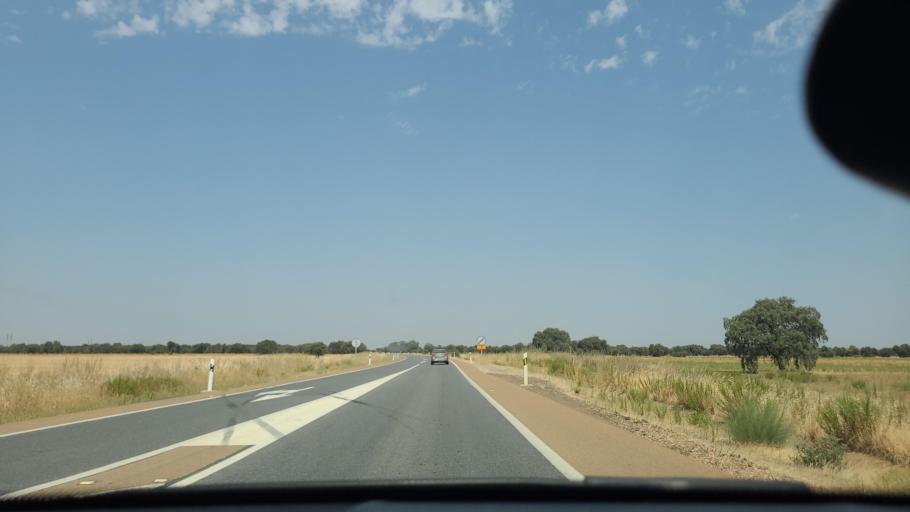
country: ES
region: Extremadura
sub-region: Provincia de Badajoz
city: Entrin Bajo
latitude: 38.6612
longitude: -6.7297
